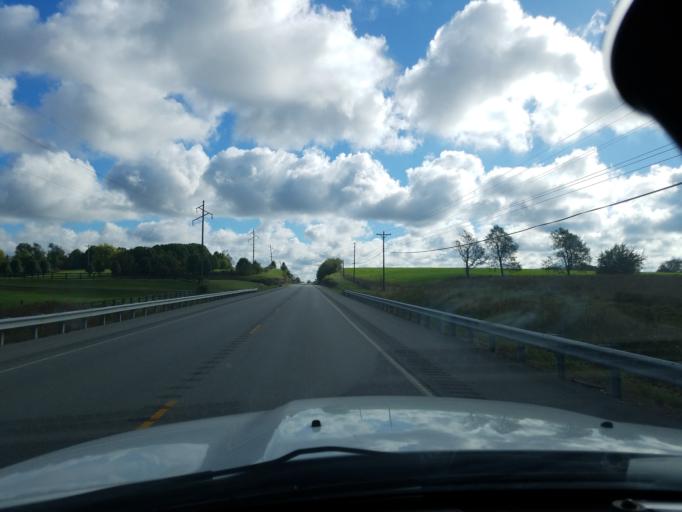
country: US
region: Kentucky
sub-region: Mercer County
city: Harrodsburg
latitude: 37.6532
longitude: -84.9289
